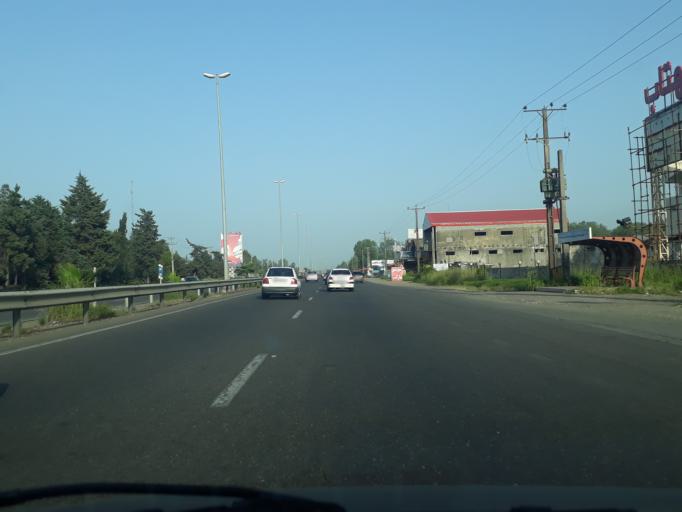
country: IR
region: Gilan
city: Bandar-e Anzali
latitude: 37.4612
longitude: 49.5690
